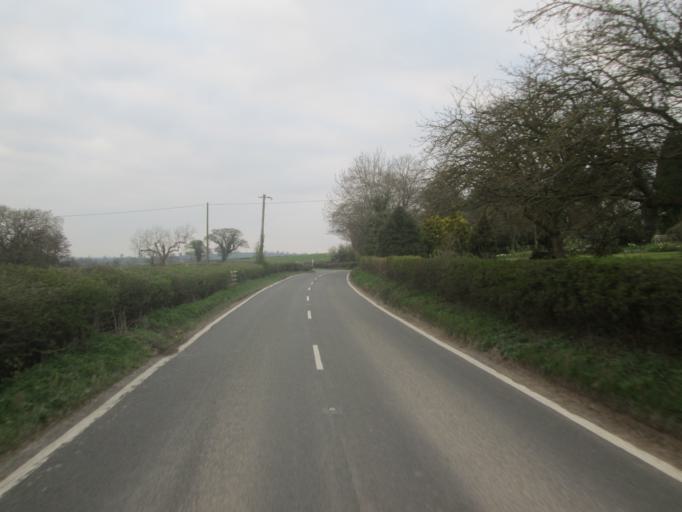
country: GB
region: England
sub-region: Derbyshire
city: Duffield
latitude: 53.0114
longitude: -1.5363
